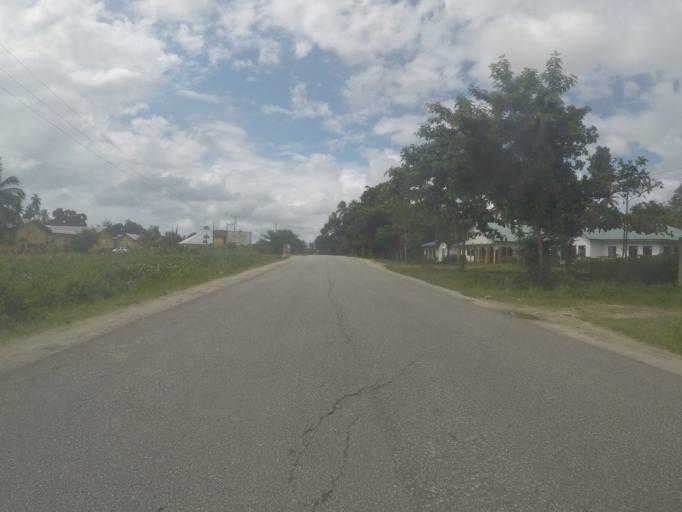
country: TZ
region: Zanzibar North
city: Mkokotoni
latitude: -5.8822
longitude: 39.2541
